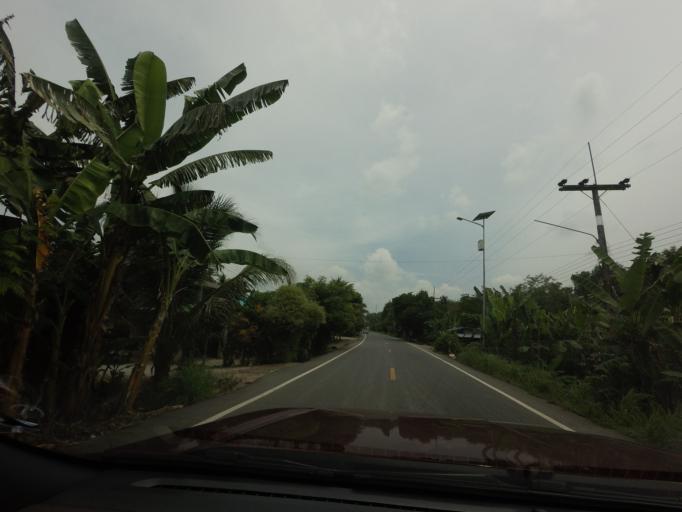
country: TH
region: Pattani
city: Yarang
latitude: 6.7137
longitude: 101.2978
